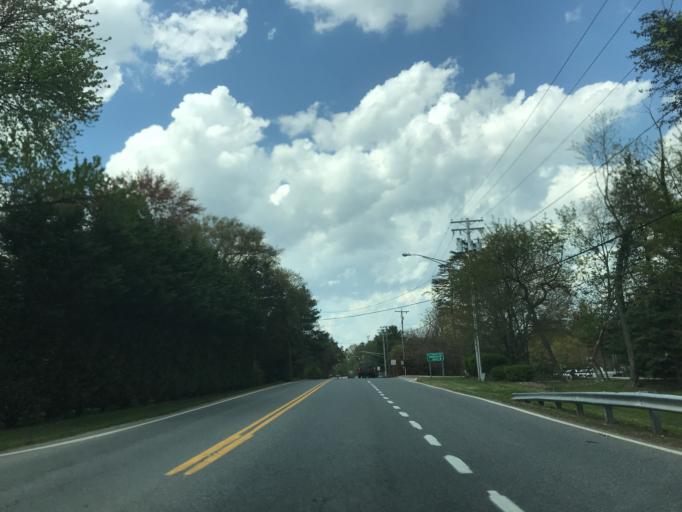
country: US
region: Maryland
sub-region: Anne Arundel County
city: Gambrills
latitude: 39.0842
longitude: -76.6763
